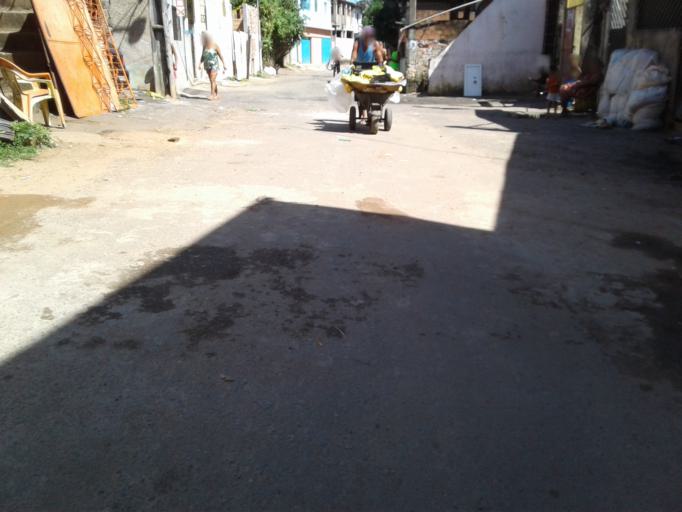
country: BR
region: Bahia
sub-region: Salvador
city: Salvador
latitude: -12.9109
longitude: -38.4688
